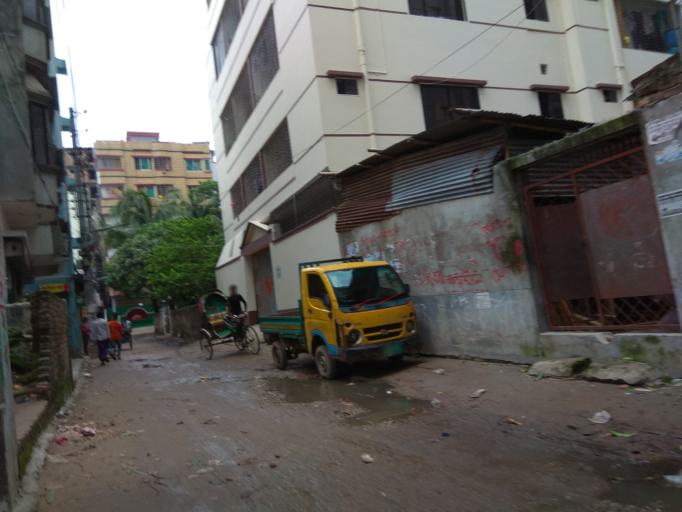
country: BD
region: Dhaka
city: Azimpur
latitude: 23.7927
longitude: 90.3690
